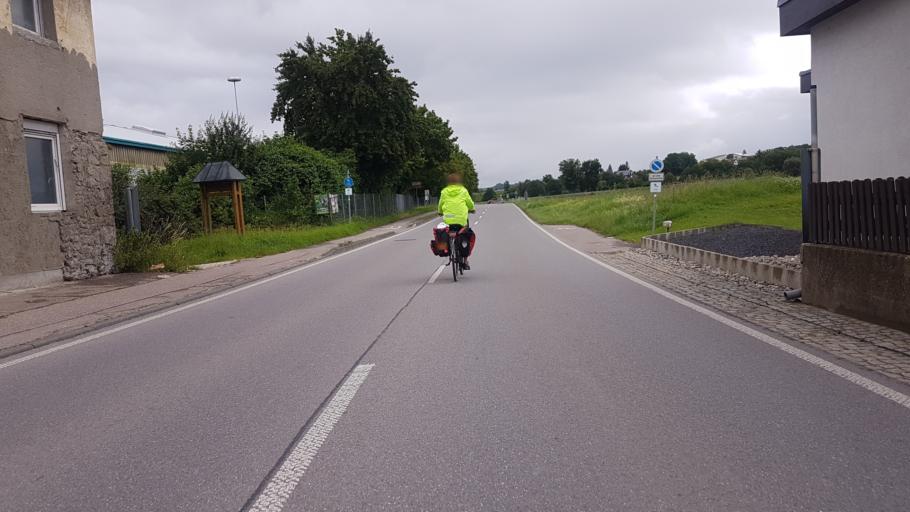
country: DE
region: Baden-Wuerttemberg
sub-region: Tuebingen Region
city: Dettingen
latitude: 48.2645
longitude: 9.7258
